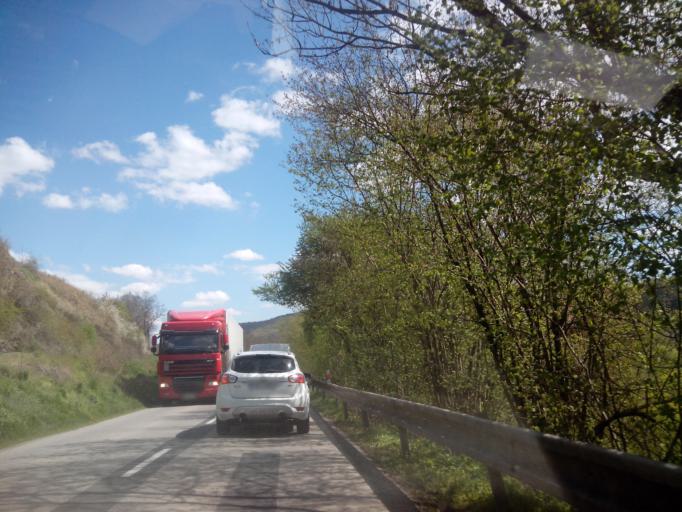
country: CZ
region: Central Bohemia
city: Hyskov
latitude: 49.9929
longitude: 14.0297
